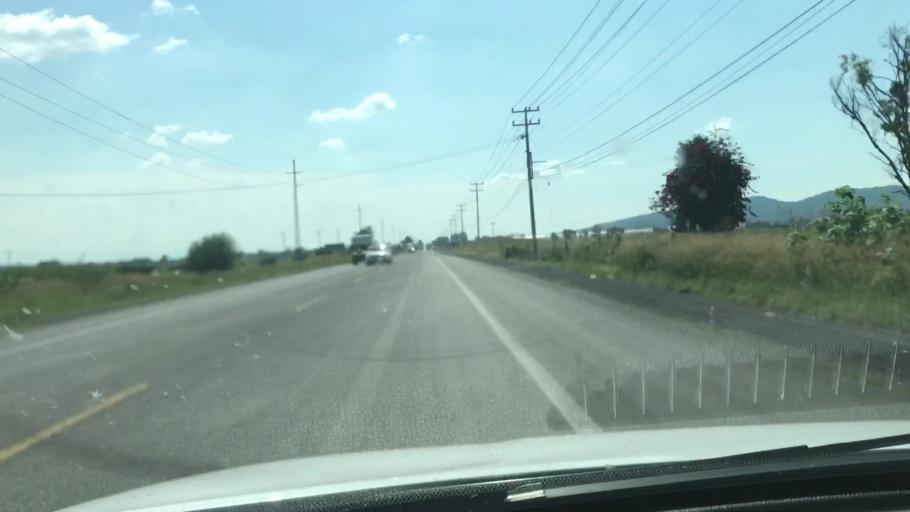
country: MX
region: Michoacan
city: Tanhuato de Guerrero
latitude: 20.2814
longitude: -102.3514
